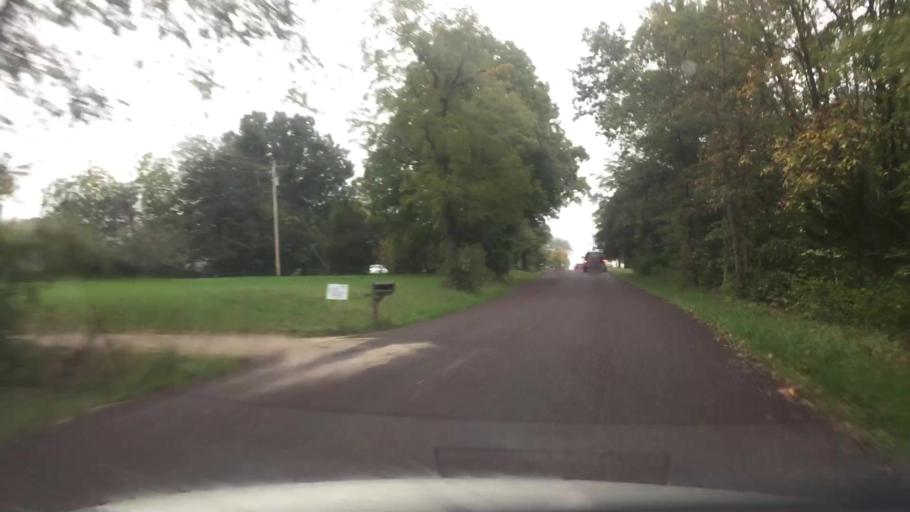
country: US
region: Missouri
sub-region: Boone County
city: Ashland
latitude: 38.8111
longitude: -92.2765
